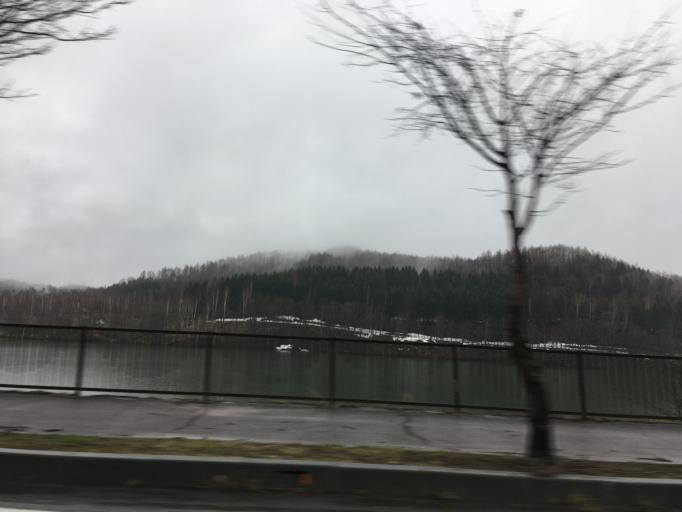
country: JP
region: Hokkaido
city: Nayoro
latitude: 44.0977
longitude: 142.4315
